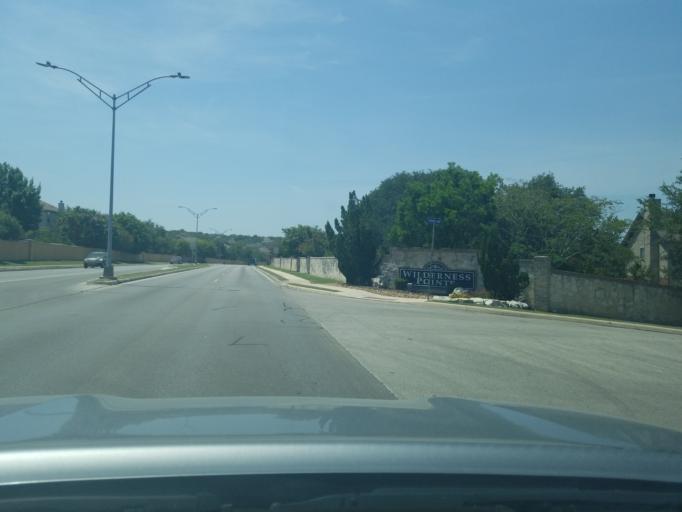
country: US
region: Texas
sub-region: Bexar County
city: Hollywood Park
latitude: 29.6507
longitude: -98.5034
